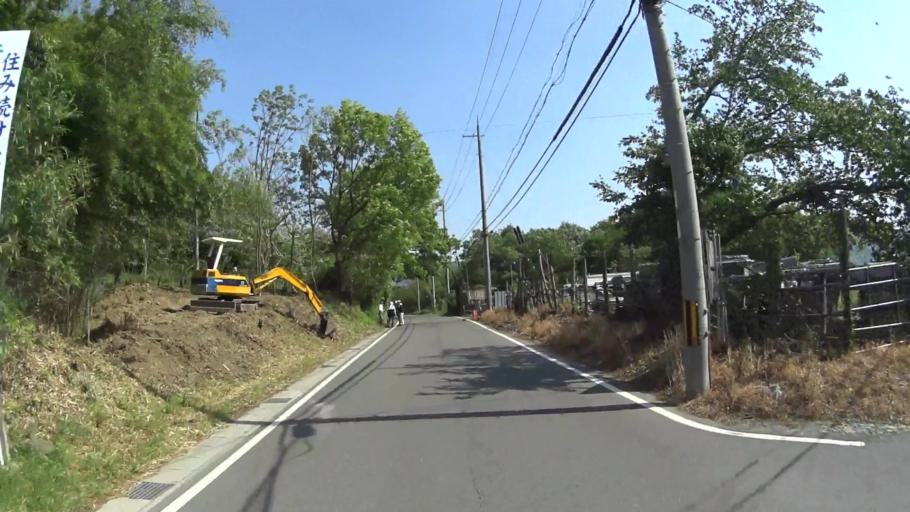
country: JP
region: Kyoto
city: Kameoka
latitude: 35.0338
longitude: 135.5868
